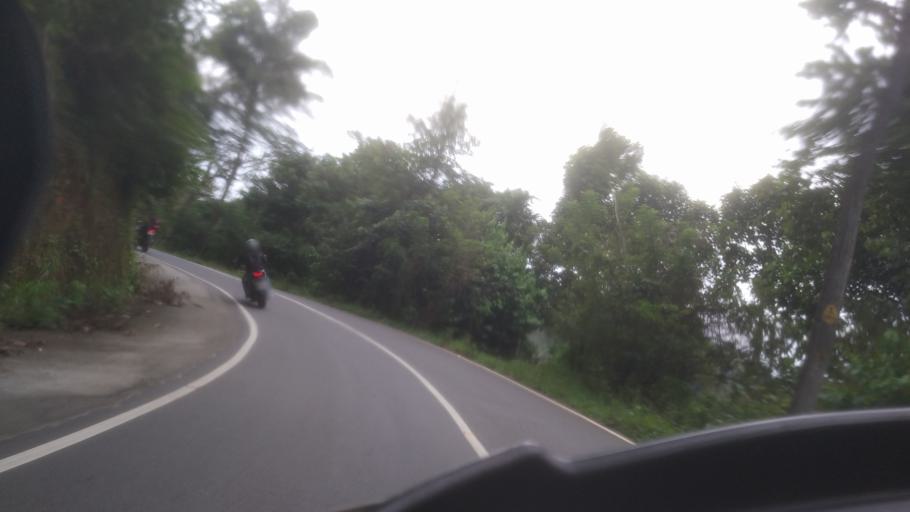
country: IN
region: Kerala
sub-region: Idukki
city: Idukki
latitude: 9.9508
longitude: 77.0118
